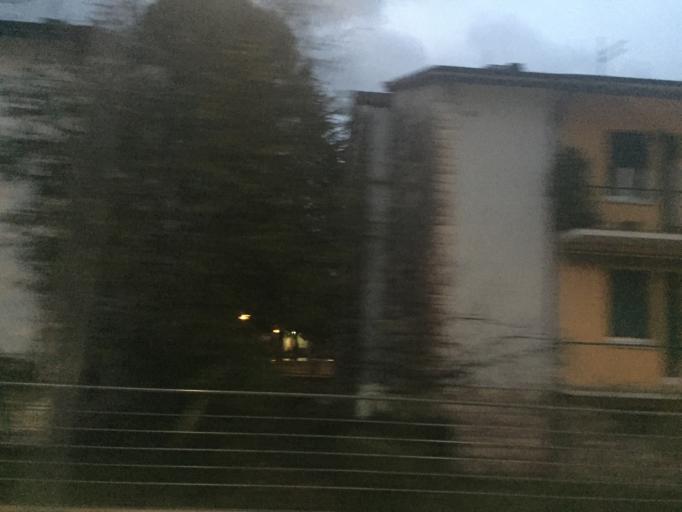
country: IT
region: The Marches
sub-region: Provincia di Macerata
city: Muccia
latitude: 43.0815
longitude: 13.0436
